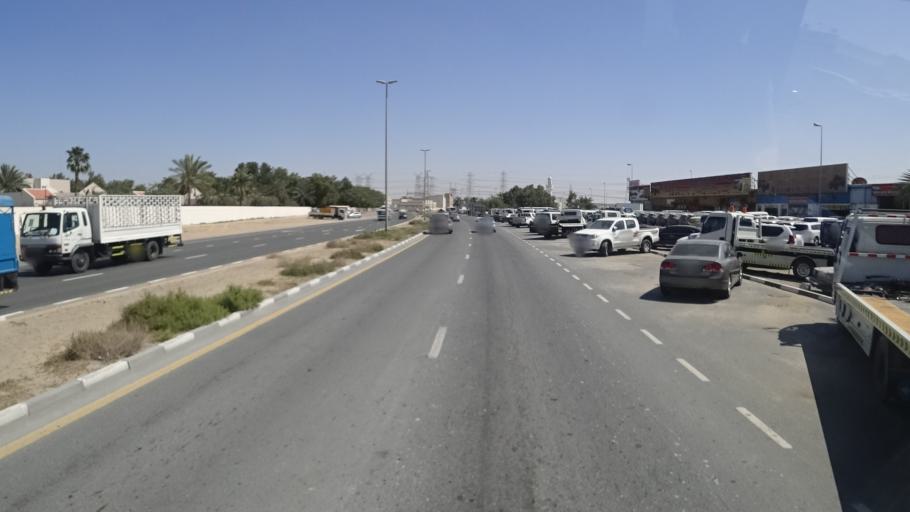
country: AE
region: Ash Shariqah
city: Sharjah
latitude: 25.1746
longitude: 55.3755
